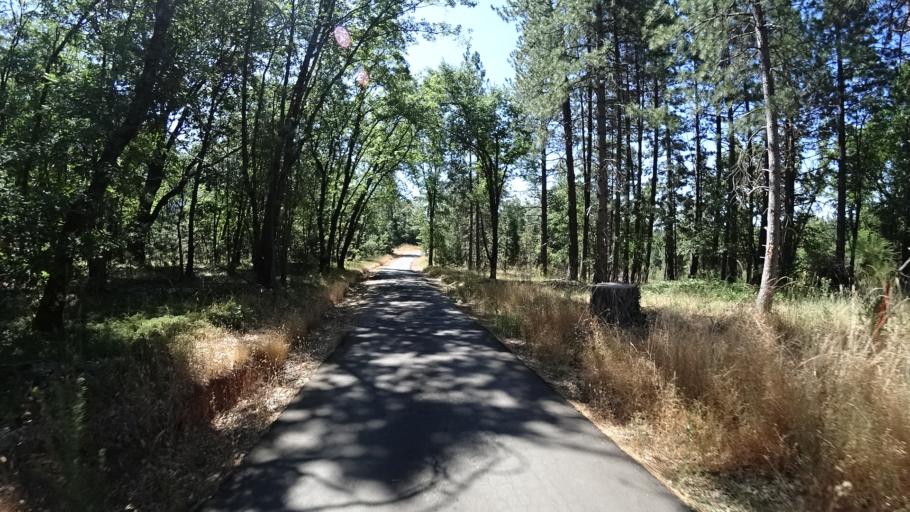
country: US
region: California
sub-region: Amador County
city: Pioneer
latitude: 38.3962
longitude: -120.5056
